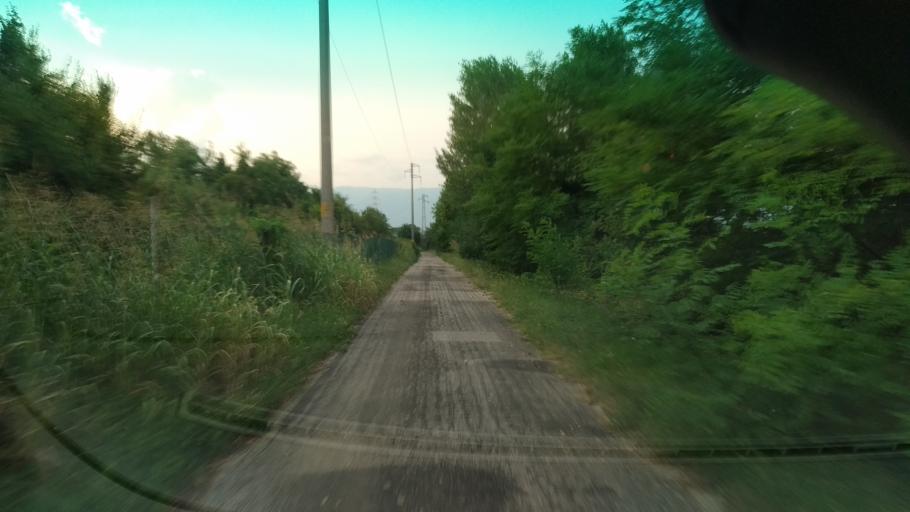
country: IT
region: Veneto
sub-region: Provincia di Vicenza
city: Montecchio Precalcino
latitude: 45.6786
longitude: 11.5635
